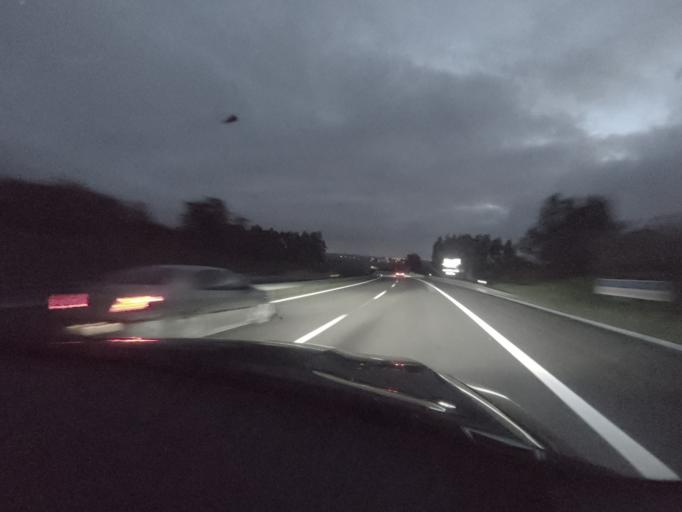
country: PT
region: Leiria
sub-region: Leiria
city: Caranguejeira
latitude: 39.7763
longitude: -8.7423
